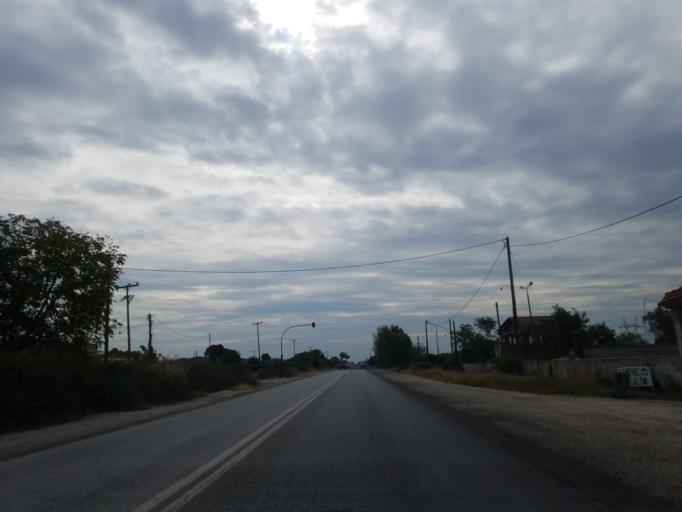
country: GR
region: Thessaly
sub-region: Trikala
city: Kalampaka
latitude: 39.6905
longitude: 21.6456
